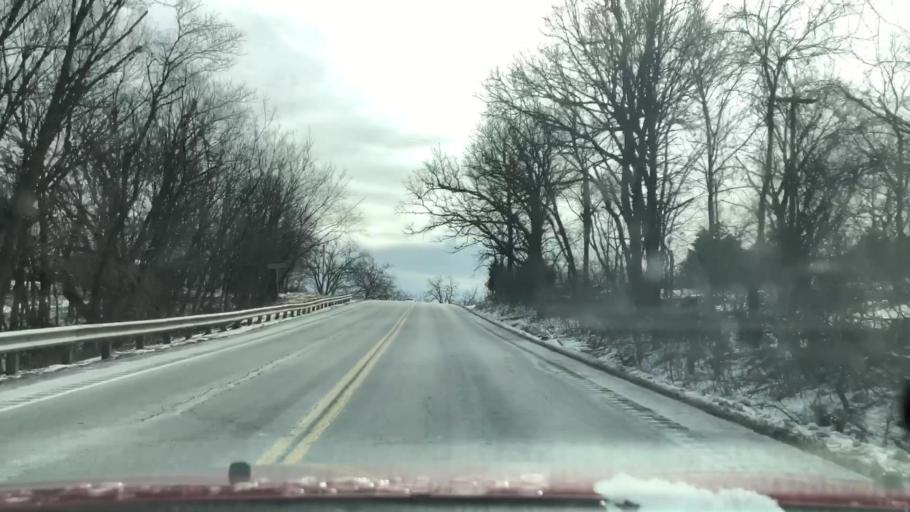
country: US
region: Missouri
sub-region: Jackson County
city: Oak Grove
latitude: 38.9349
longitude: -94.1334
